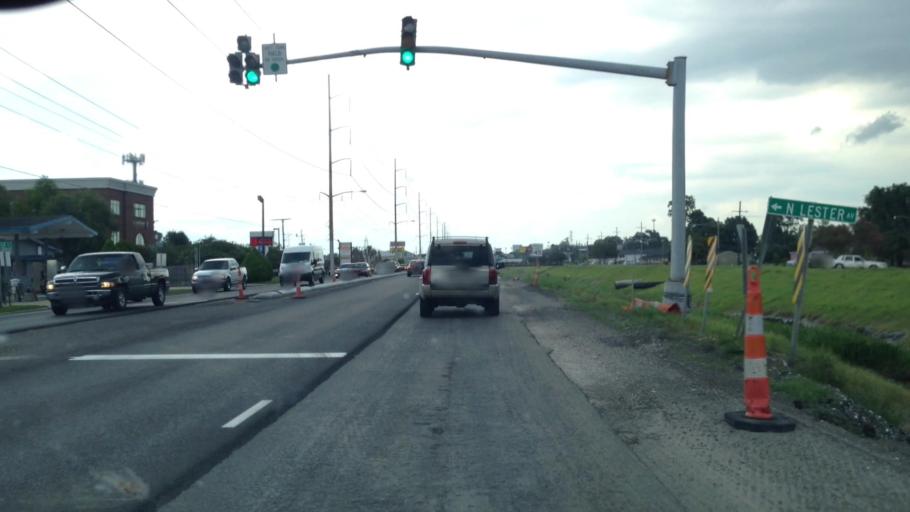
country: US
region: Louisiana
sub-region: Jefferson Parish
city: River Ridge
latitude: 29.9784
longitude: -90.2208
